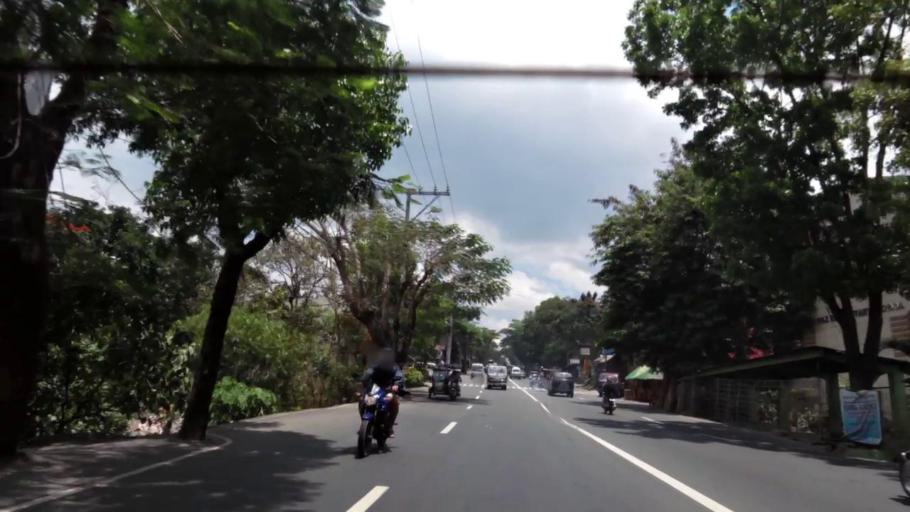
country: PH
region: Calabarzon
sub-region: Province of Rizal
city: Cainta
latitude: 14.5974
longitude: 121.1723
